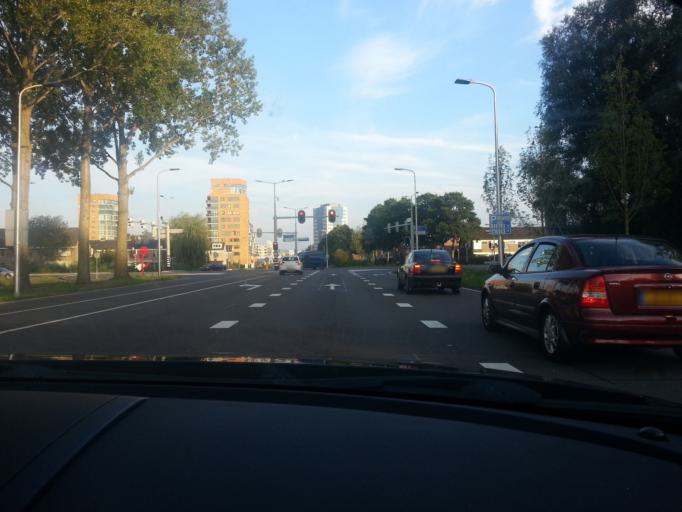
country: NL
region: South Holland
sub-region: Gemeente Capelle aan den IJssel
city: Capelle aan den IJssel
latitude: 51.9341
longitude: 4.5830
